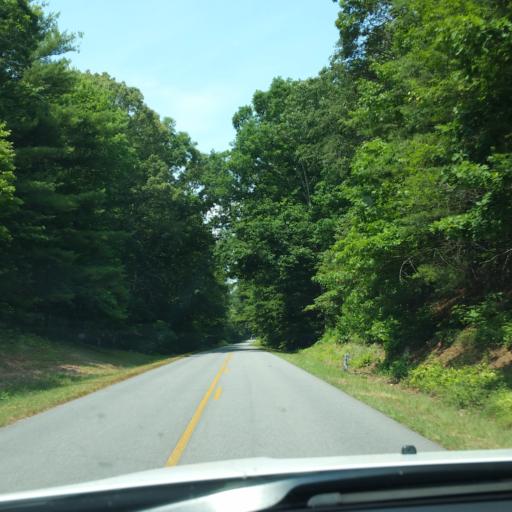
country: US
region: North Carolina
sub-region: Buncombe County
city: Biltmore Forest
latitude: 35.5134
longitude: -82.5475
